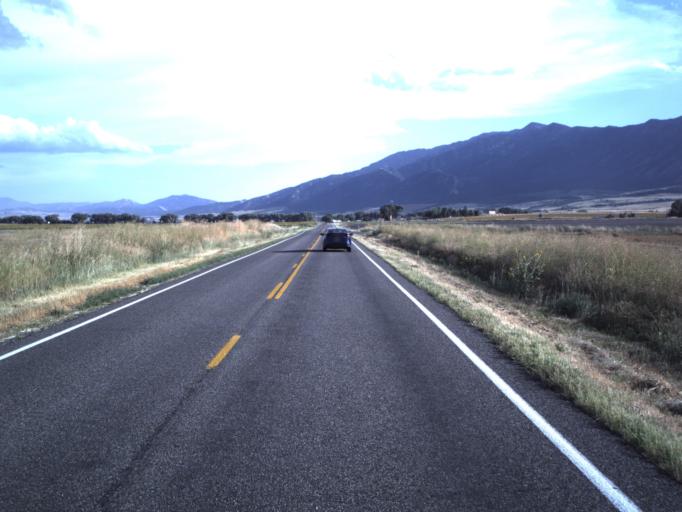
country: US
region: Utah
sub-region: Cache County
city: Mendon
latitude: 41.7587
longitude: -111.9794
